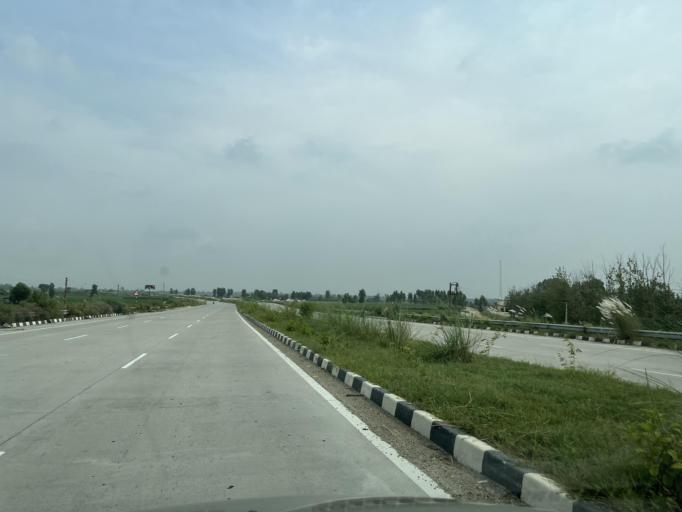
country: IN
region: Uttarakhand
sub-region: Udham Singh Nagar
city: Bazpur
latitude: 29.1500
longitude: 79.0239
